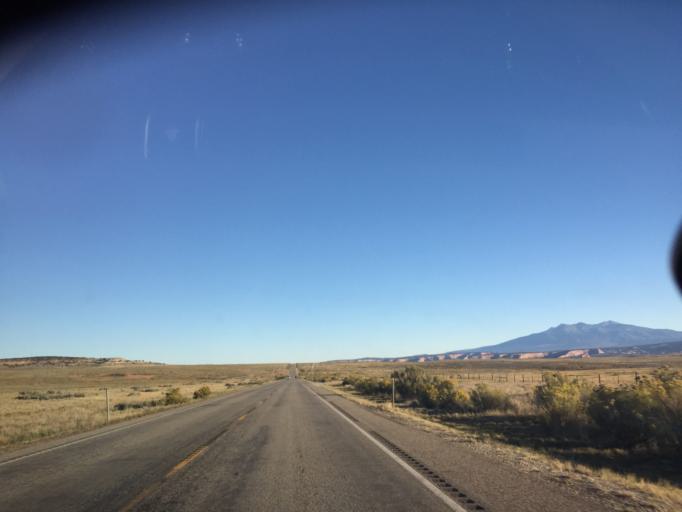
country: US
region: Utah
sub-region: San Juan County
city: Monticello
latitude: 38.1110
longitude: -109.3643
